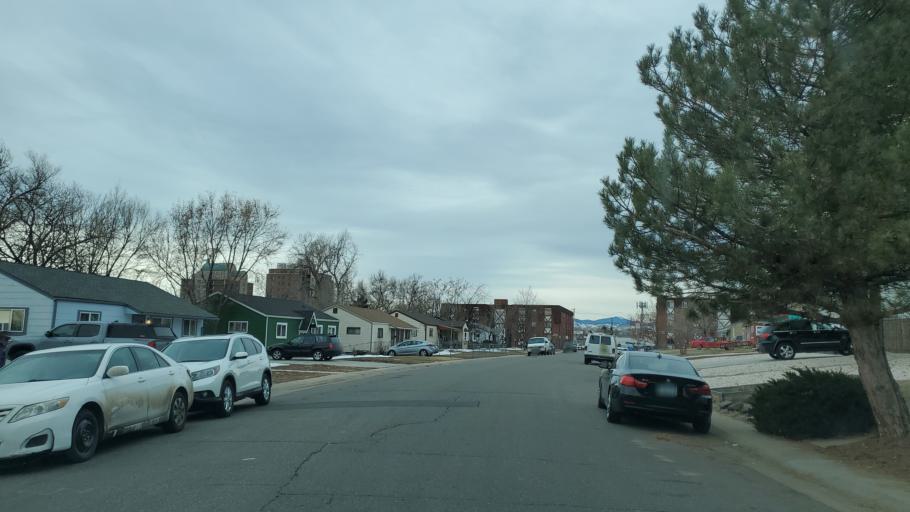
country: US
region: Colorado
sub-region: Denver County
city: Denver
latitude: 39.6974
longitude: -105.0049
